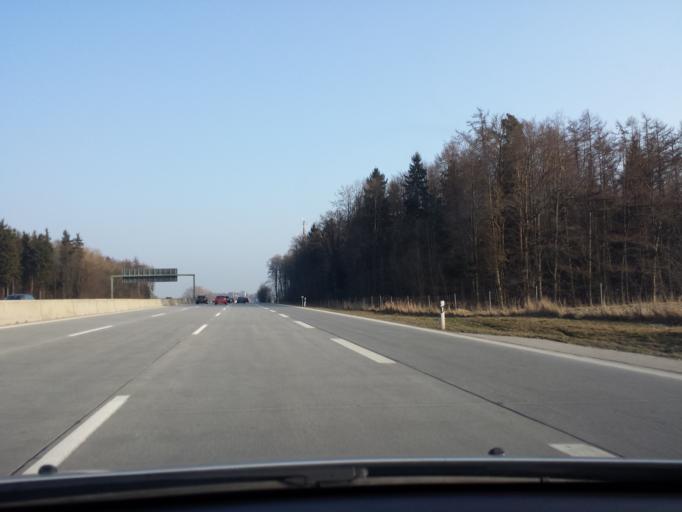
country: DE
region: Bavaria
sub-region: Upper Bavaria
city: Sulzemoos
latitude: 48.2786
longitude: 11.2744
